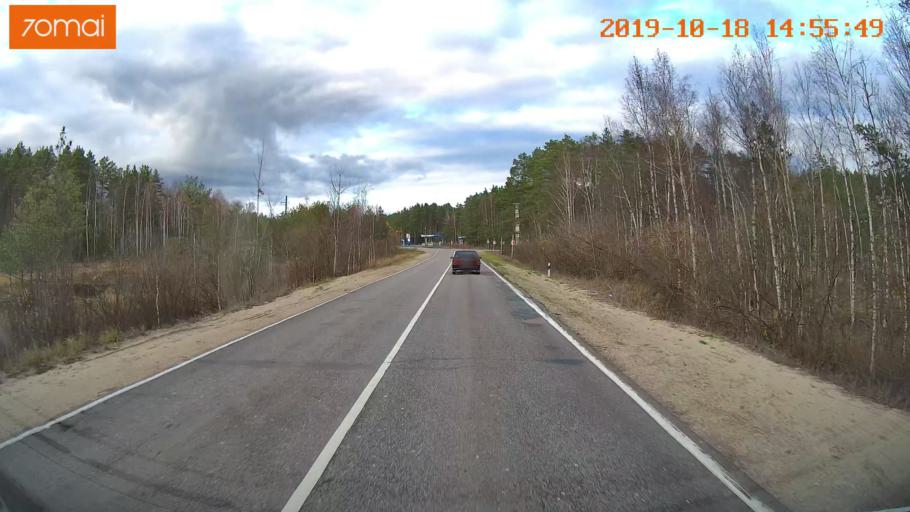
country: RU
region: Vladimir
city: Kurlovo
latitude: 55.4575
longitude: 40.5896
